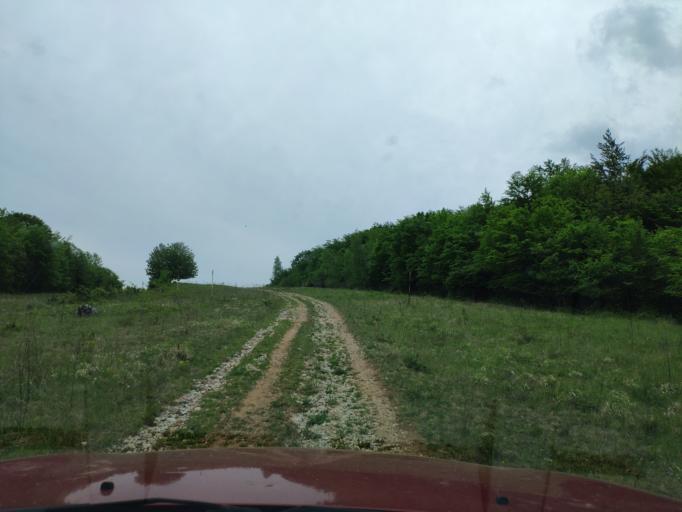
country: SK
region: Kosicky
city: Roznava
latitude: 48.5434
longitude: 20.5896
